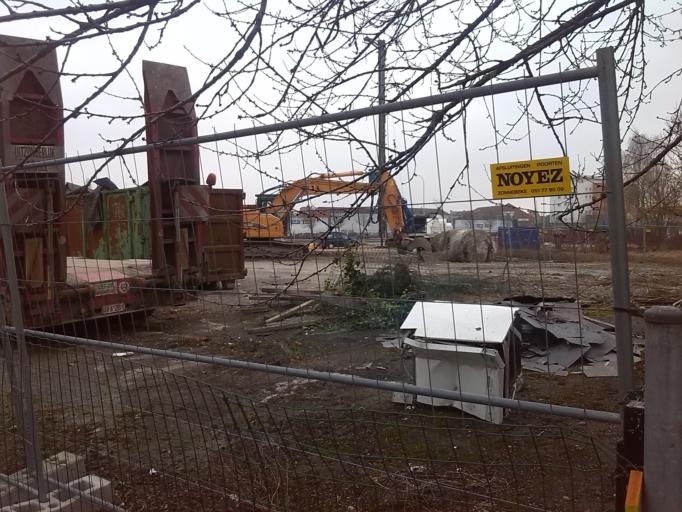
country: BE
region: Flanders
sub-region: Provincie West-Vlaanderen
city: Brugge
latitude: 51.2230
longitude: 3.2208
